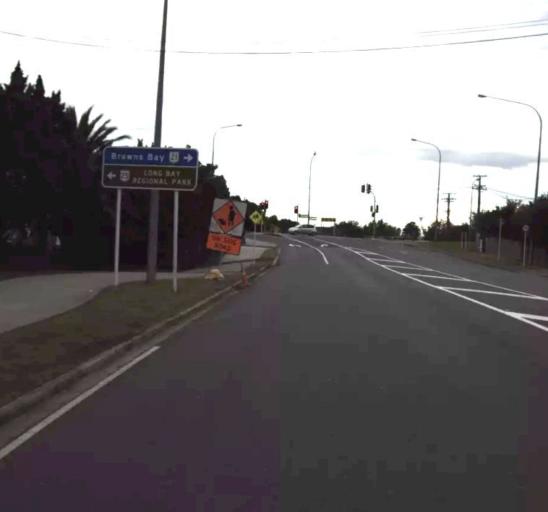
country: NZ
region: Auckland
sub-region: Auckland
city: Rothesay Bay
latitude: -36.7283
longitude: 174.7272
